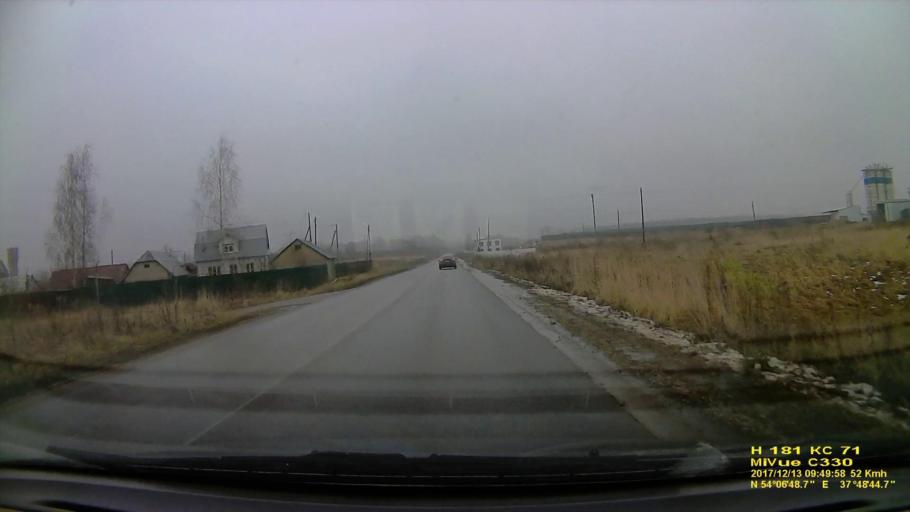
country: RU
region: Tula
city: Bolokhovo
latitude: 54.1136
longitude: 37.8126
